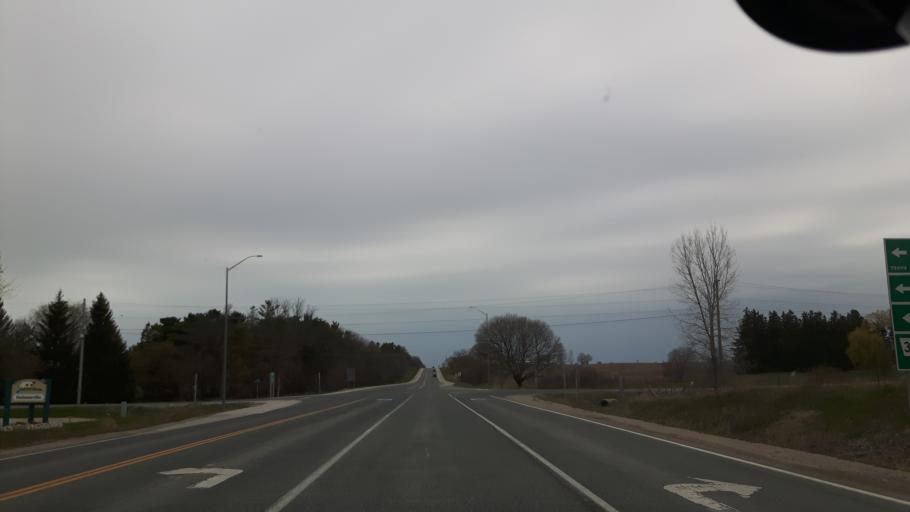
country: CA
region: Ontario
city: Goderich
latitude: 43.6462
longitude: -81.6009
